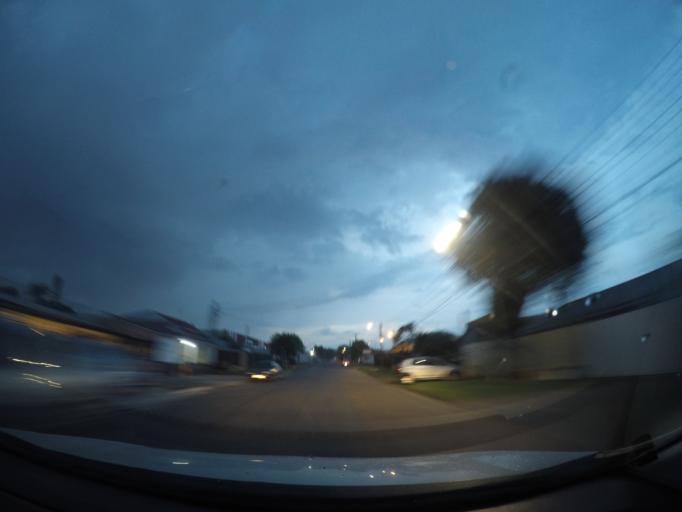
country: BR
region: Parana
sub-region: Sao Jose Dos Pinhais
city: Sao Jose dos Pinhais
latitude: -25.5179
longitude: -49.2255
